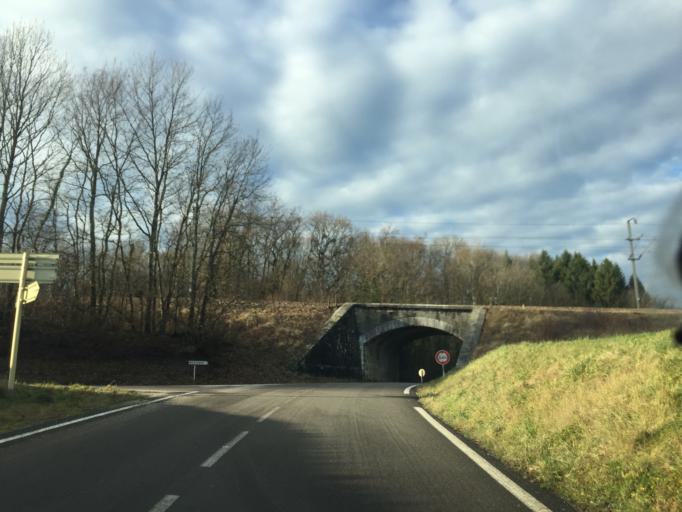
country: FR
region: Franche-Comte
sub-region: Departement du Jura
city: Mouchard
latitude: 46.9531
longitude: 5.7856
